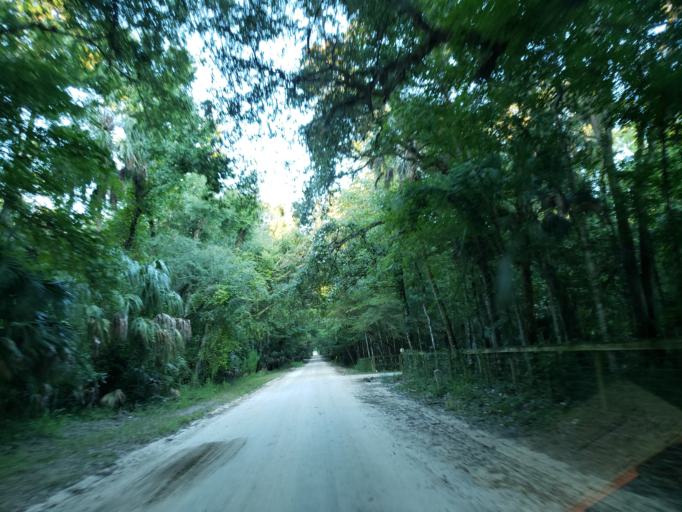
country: US
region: Florida
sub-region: Alachua County
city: Gainesville
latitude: 29.4842
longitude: -82.2743
